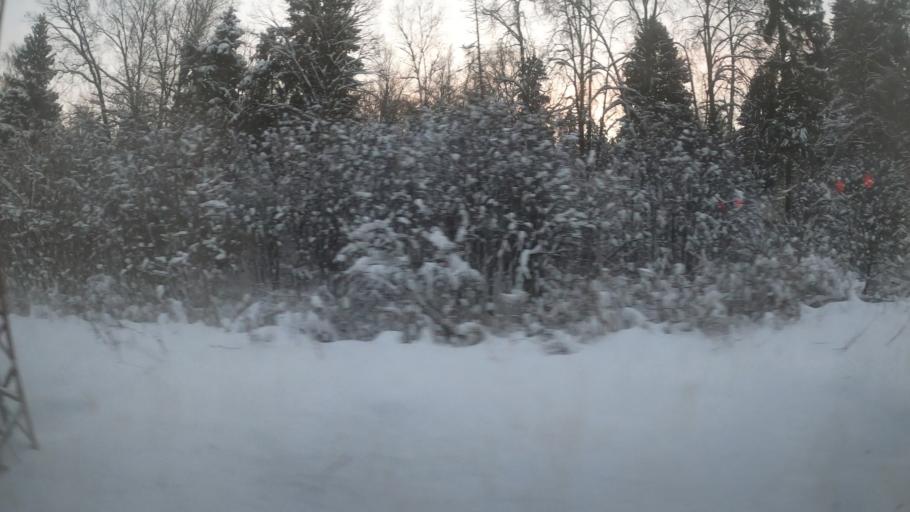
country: RU
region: Moskovskaya
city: Lugovaya
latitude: 56.0621
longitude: 37.4887
